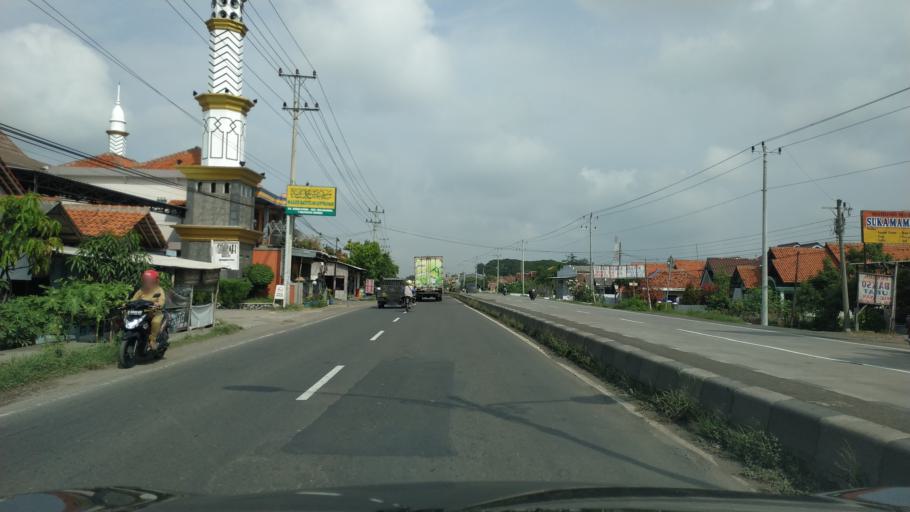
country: ID
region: Central Java
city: Bulakamba
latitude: -6.8744
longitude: 108.9370
